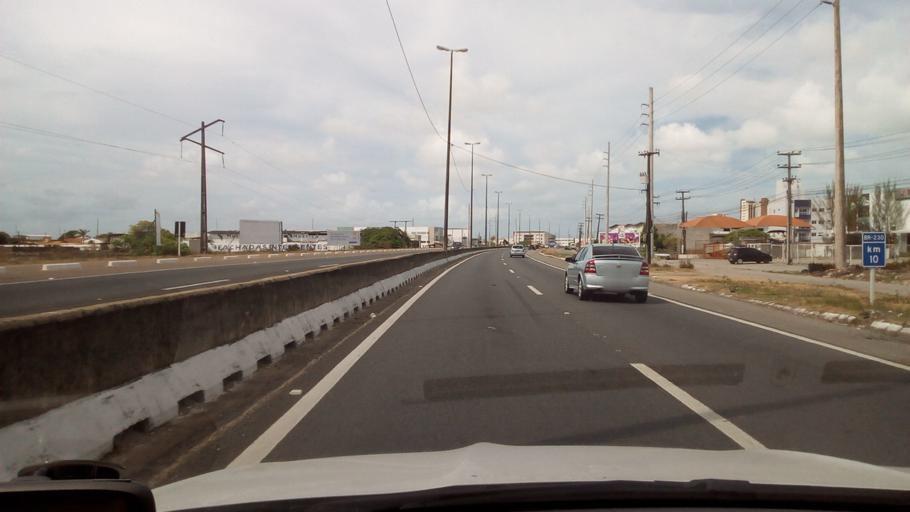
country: BR
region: Paraiba
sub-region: Joao Pessoa
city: Joao Pessoa
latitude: -7.0540
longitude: -34.8504
